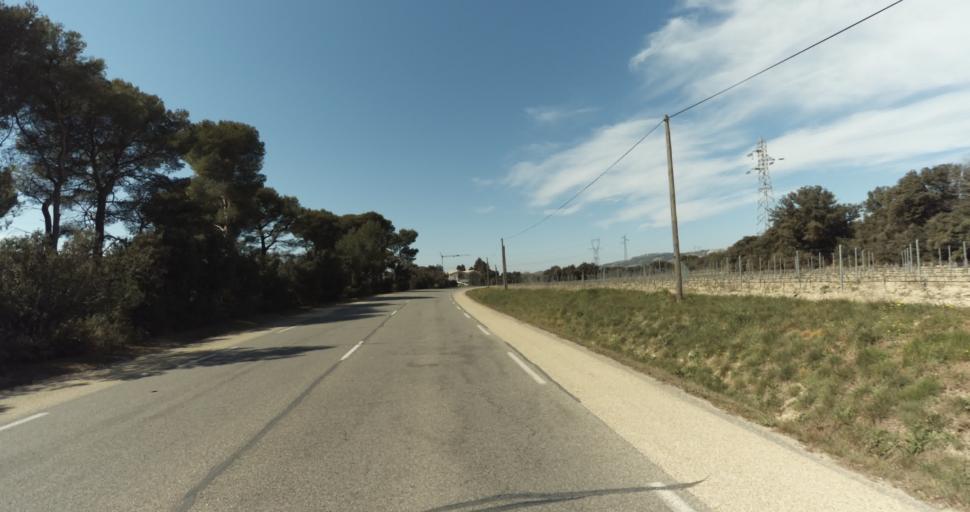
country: FR
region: Provence-Alpes-Cote d'Azur
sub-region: Departement des Bouches-du-Rhone
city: Pelissanne
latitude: 43.6437
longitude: 5.1959
